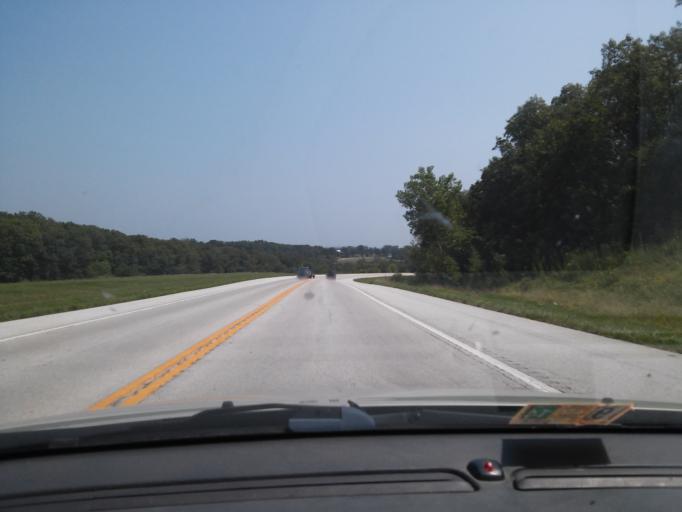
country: US
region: Missouri
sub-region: Pike County
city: Bowling Green
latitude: 39.3625
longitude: -91.1976
